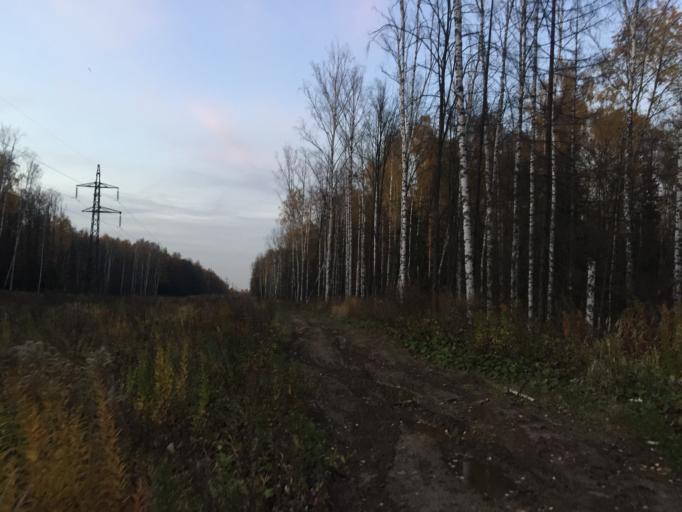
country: RU
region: Moskovskaya
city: Druzhba
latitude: 55.8711
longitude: 37.7674
